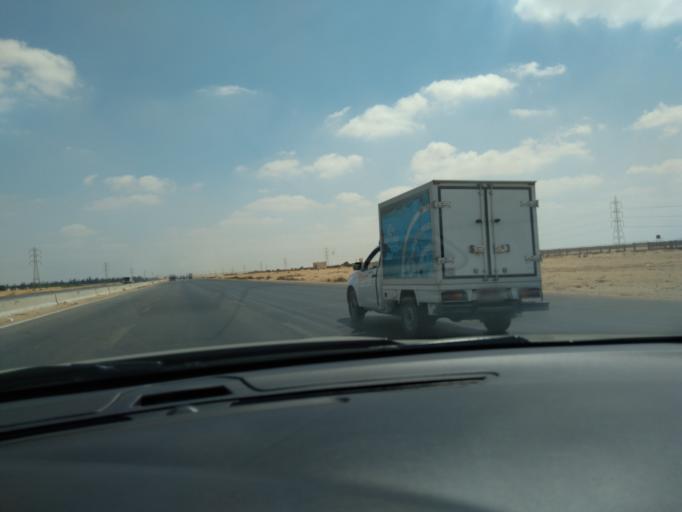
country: EG
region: Al Isma'iliyah
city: At Tall al Kabir
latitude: 30.3519
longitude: 31.8875
